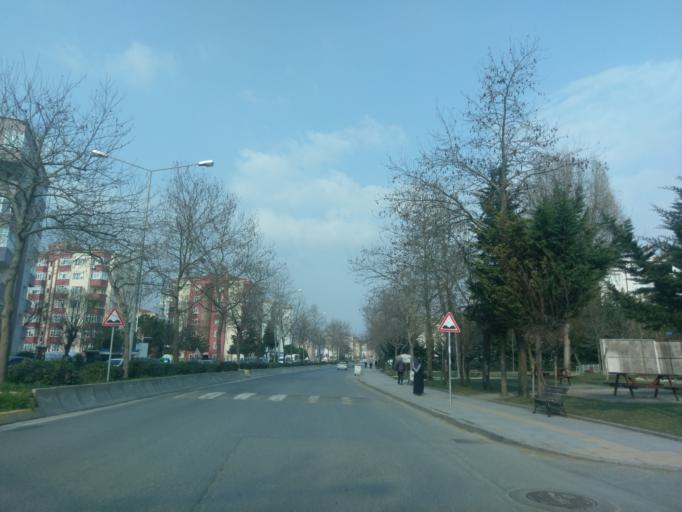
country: TR
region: Istanbul
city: Silivri
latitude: 41.0789
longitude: 28.2555
